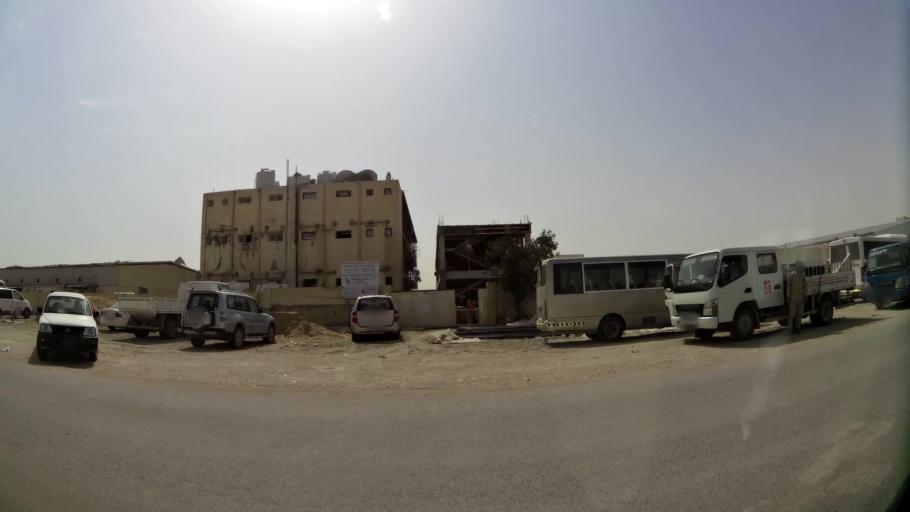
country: QA
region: Al Wakrah
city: Al Wukayr
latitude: 25.1709
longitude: 51.4660
